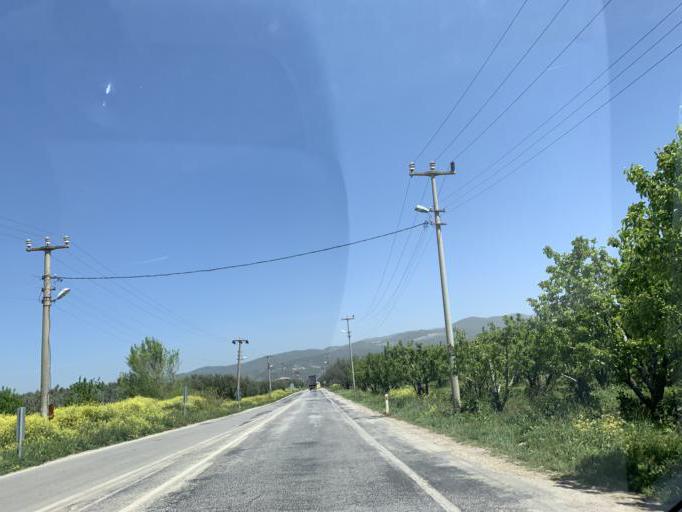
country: TR
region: Bursa
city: Iznik
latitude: 40.4125
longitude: 29.7097
